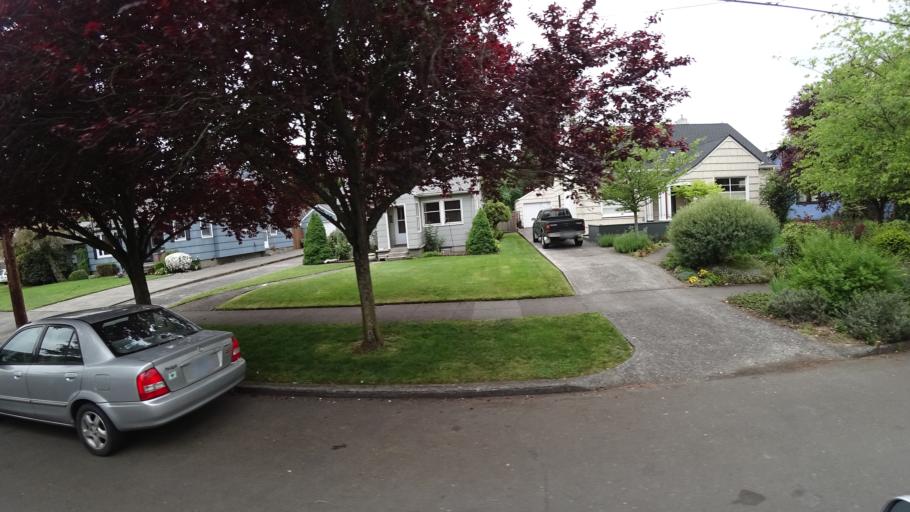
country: US
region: Oregon
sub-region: Multnomah County
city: Portland
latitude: 45.5493
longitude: -122.6172
